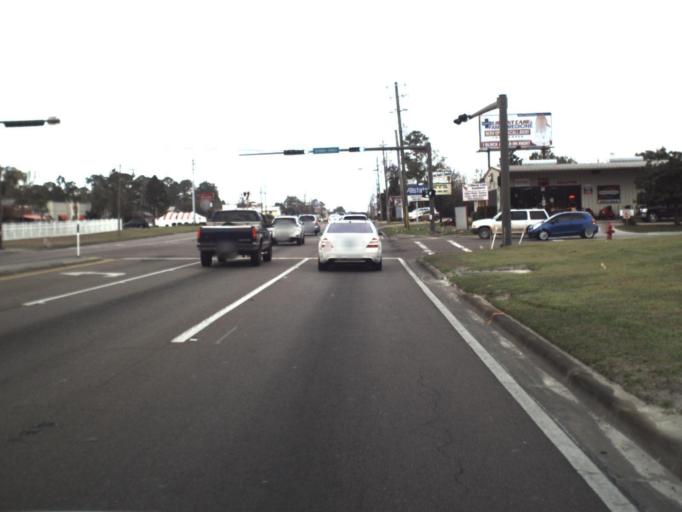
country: US
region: Florida
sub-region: Bay County
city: Springfield
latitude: 30.1606
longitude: -85.5912
